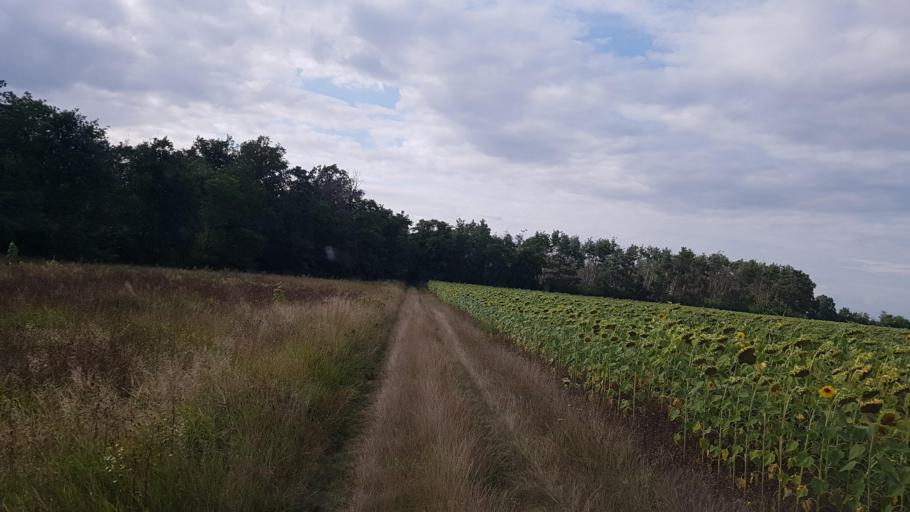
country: DE
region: Brandenburg
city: Muhlberg
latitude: 51.4926
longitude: 13.2648
